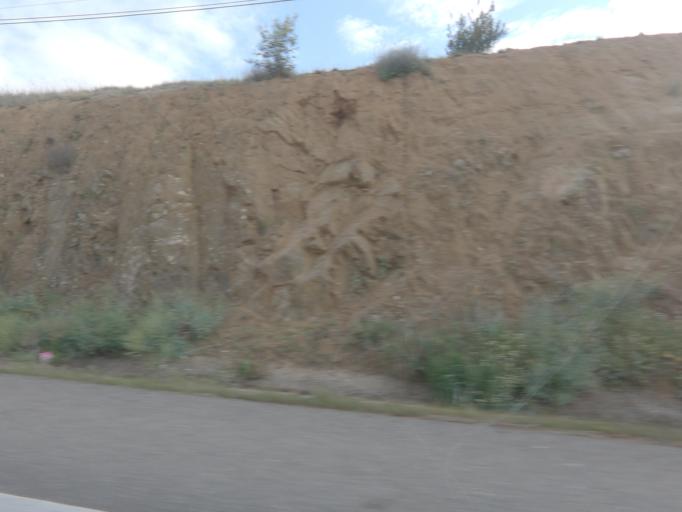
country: ES
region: Extremadura
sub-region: Provincia de Caceres
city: Canaveral
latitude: 39.8258
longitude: -6.3745
